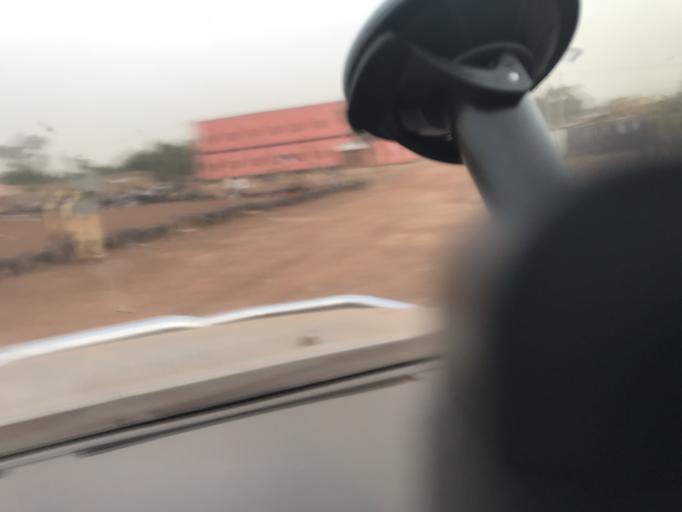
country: ML
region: Bamako
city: Bamako
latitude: 12.6533
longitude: -7.8876
